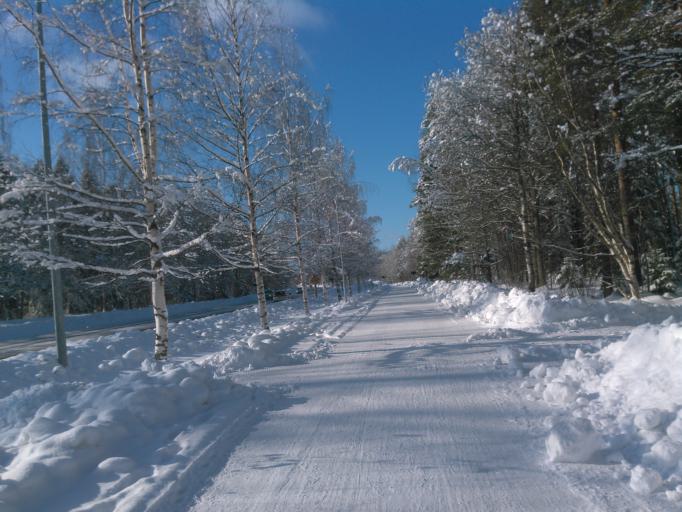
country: SE
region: Vaesterbotten
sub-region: Umea Kommun
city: Umea
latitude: 63.8141
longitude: 20.3220
